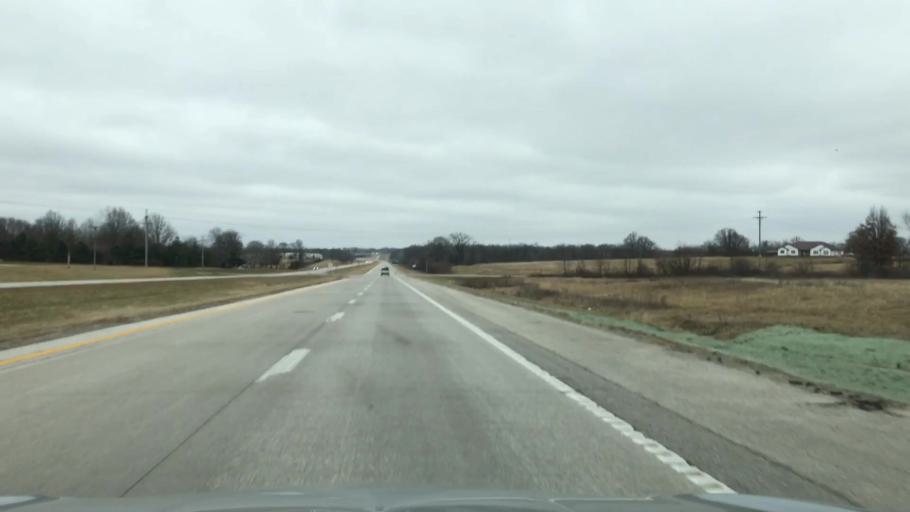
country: US
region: Missouri
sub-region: Linn County
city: Brookfield
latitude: 39.7792
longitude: -93.1015
